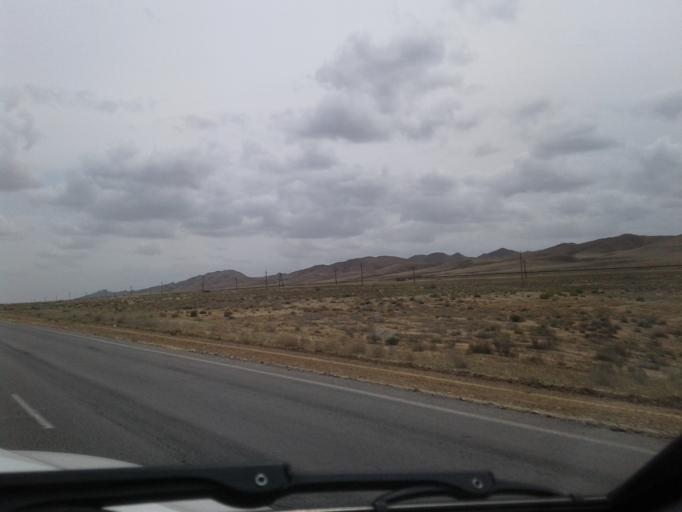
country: IR
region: Razavi Khorasan
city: Dargaz
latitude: 37.6262
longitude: 59.1645
